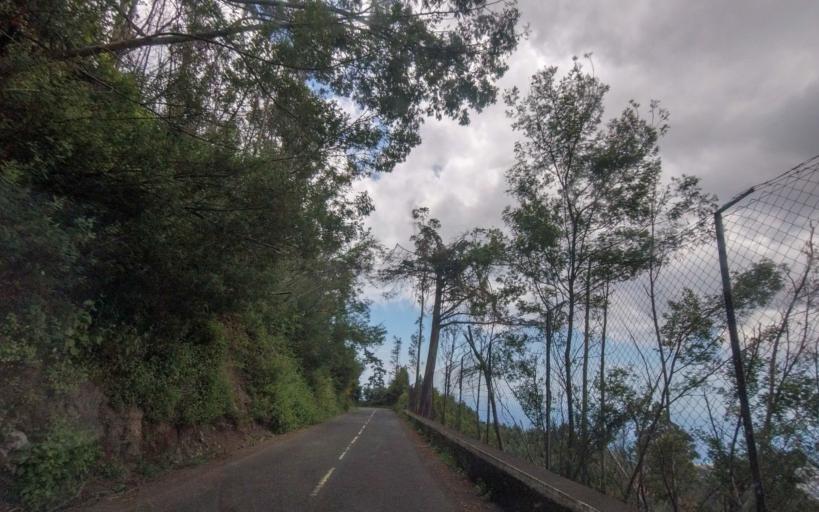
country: PT
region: Madeira
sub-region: Funchal
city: Nossa Senhora do Monte
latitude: 32.6748
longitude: -16.8845
